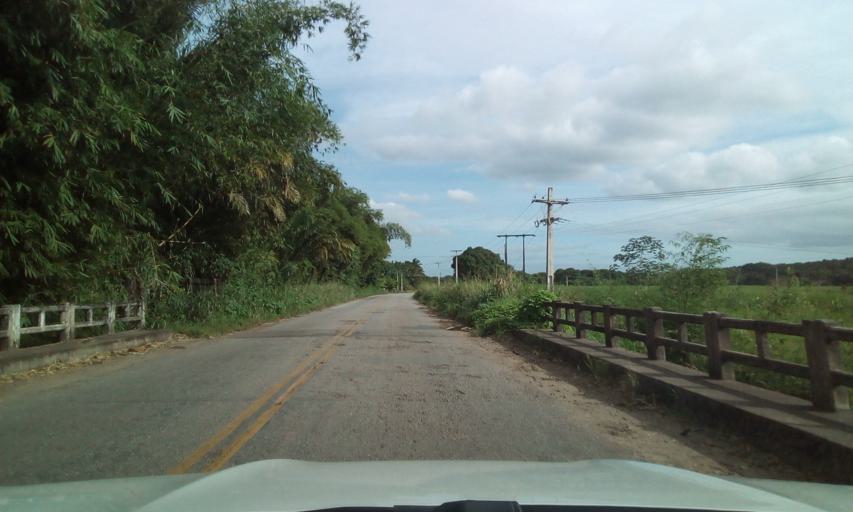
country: BR
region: Paraiba
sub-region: Cabedelo
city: Cabedelo
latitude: -6.9575
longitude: -34.9414
